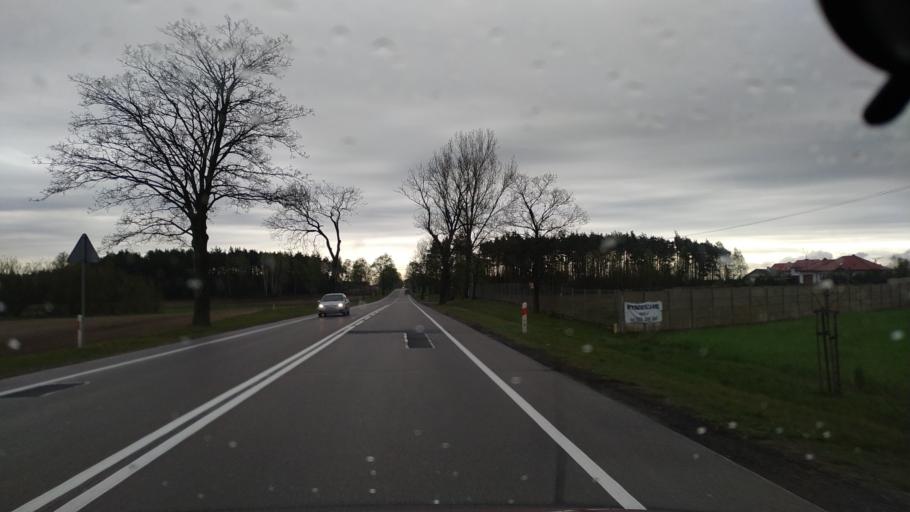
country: PL
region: Pomeranian Voivodeship
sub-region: Powiat chojnicki
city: Czersk
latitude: 53.8073
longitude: 18.0196
